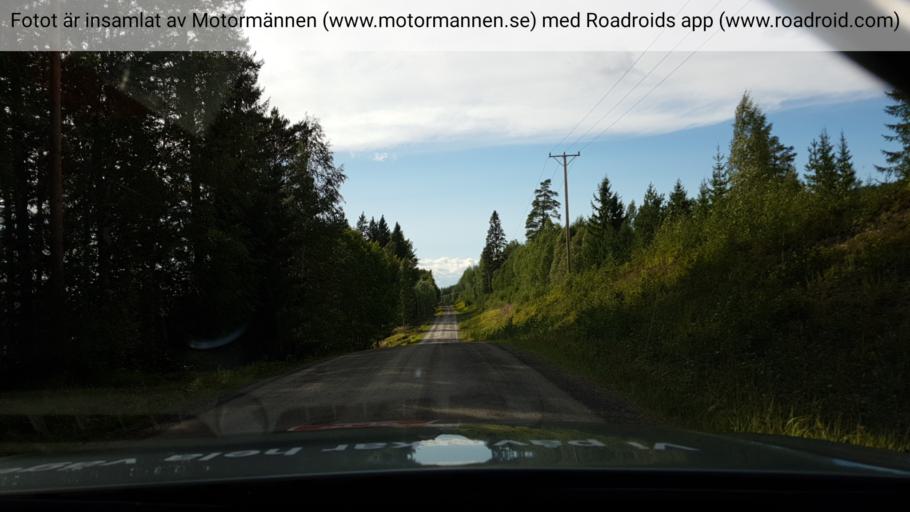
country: SE
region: Jaemtland
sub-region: Braecke Kommun
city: Braecke
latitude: 63.1959
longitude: 15.4913
